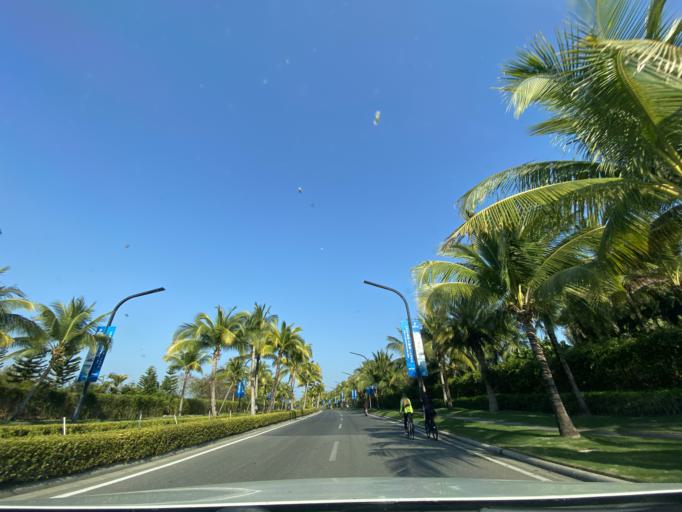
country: CN
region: Hainan
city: Xincun
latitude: 18.4220
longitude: 109.9485
